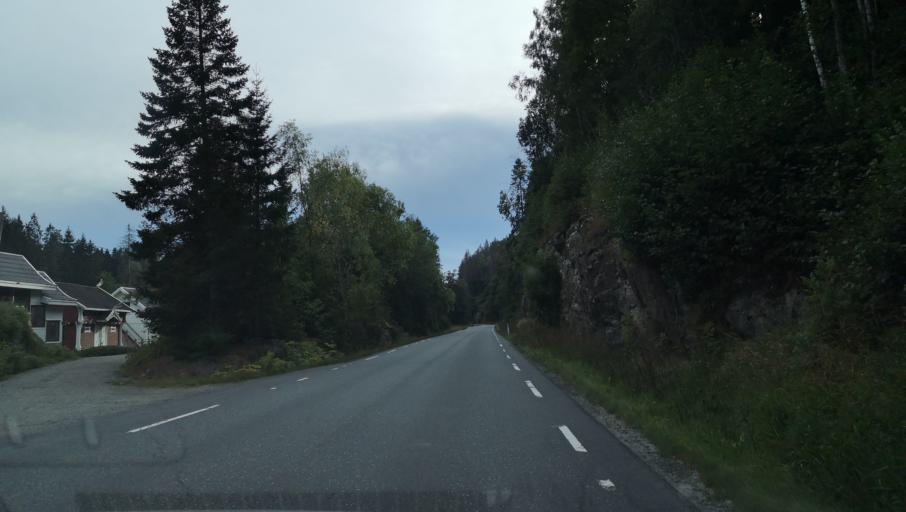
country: NO
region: Ostfold
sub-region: Hobol
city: Tomter
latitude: 59.6754
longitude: 11.0263
